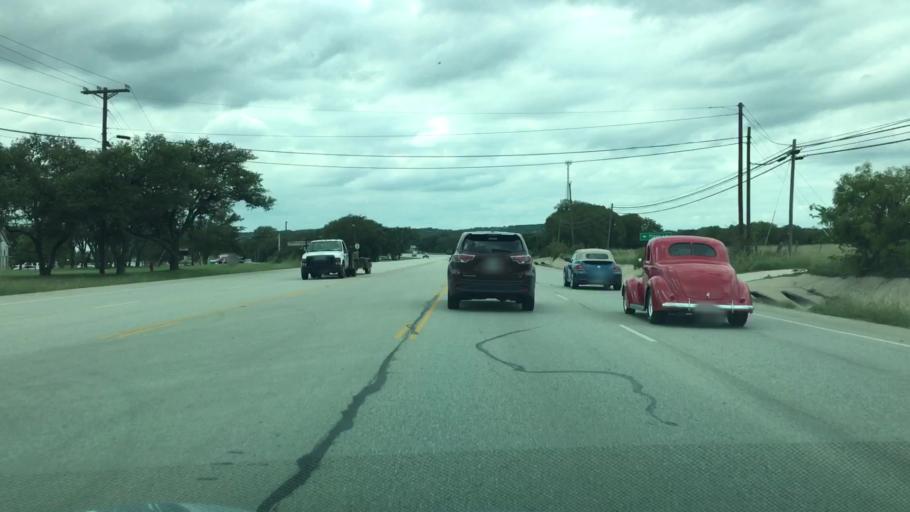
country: US
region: Texas
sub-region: Hays County
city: Dripping Springs
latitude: 30.2024
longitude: -98.1125
